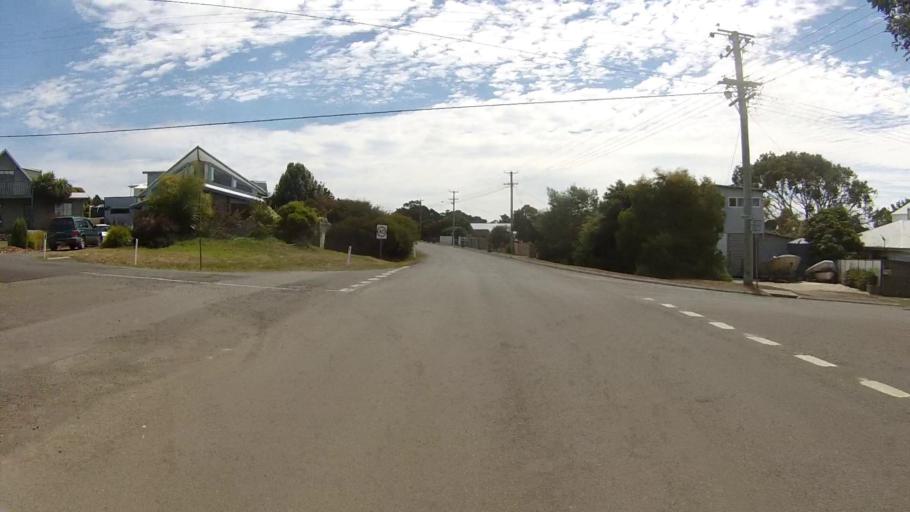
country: AU
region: Tasmania
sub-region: Clarence
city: Sandford
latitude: -42.9911
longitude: 147.5231
